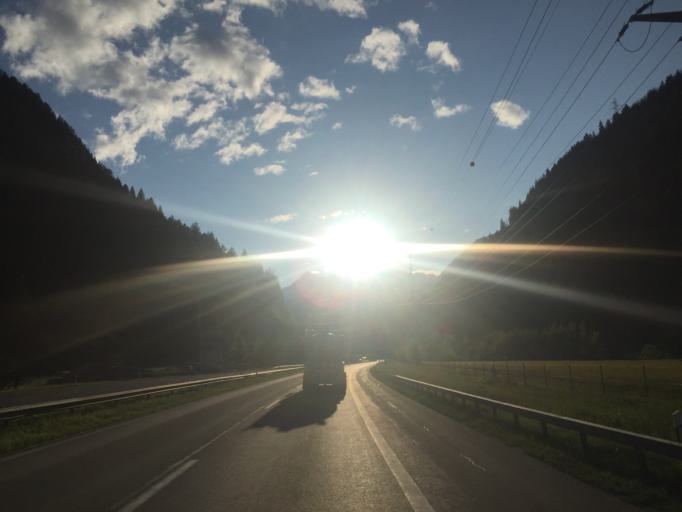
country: CH
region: Ticino
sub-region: Leventina District
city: Airolo
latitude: 46.5164
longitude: 8.6604
